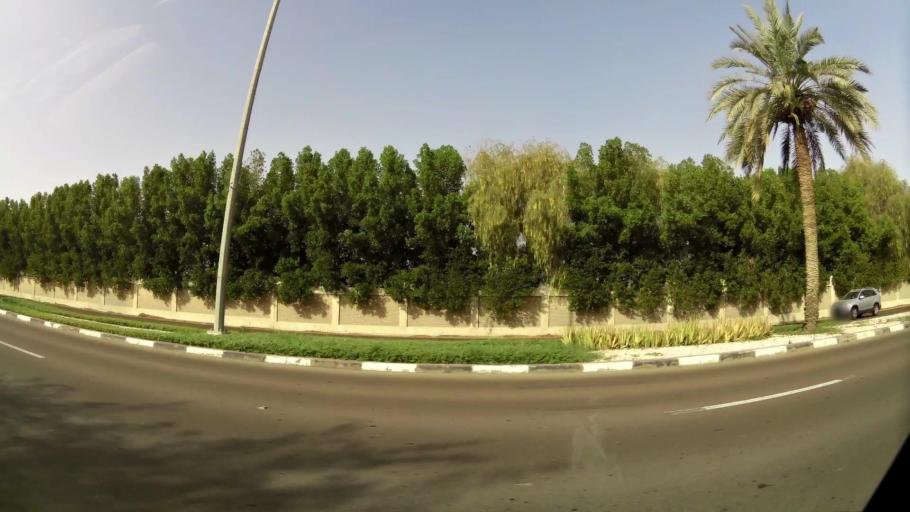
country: AE
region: Abu Dhabi
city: Al Ain
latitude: 24.2044
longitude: 55.6886
